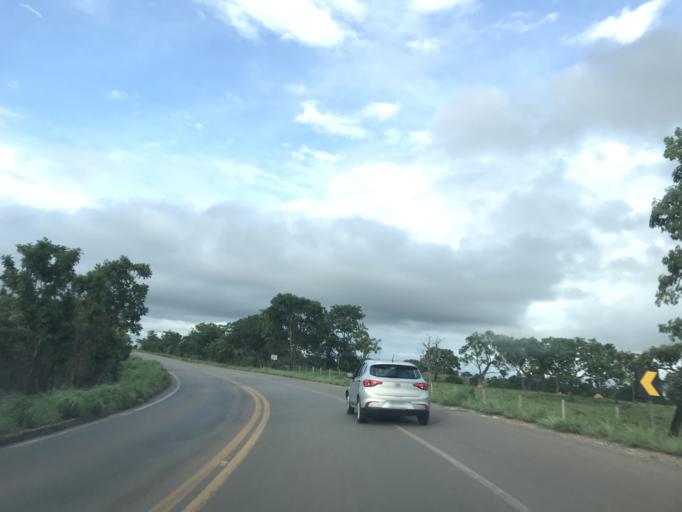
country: BR
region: Goias
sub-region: Luziania
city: Luziania
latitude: -16.3943
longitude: -48.1651
